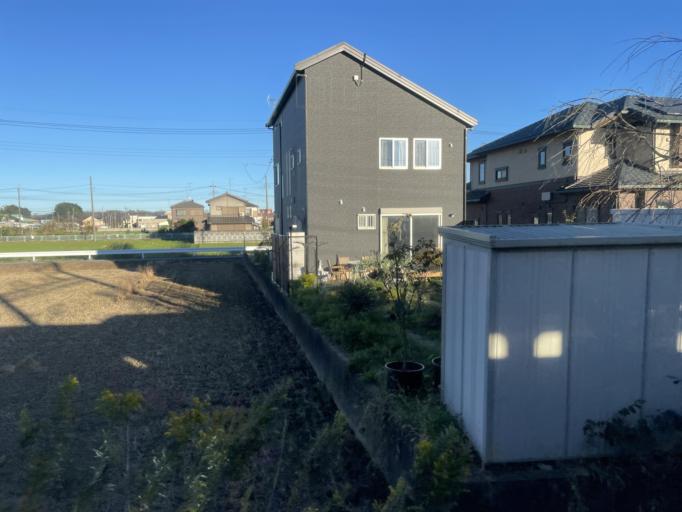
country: JP
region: Saitama
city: Satte
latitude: 36.0904
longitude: 139.7177
